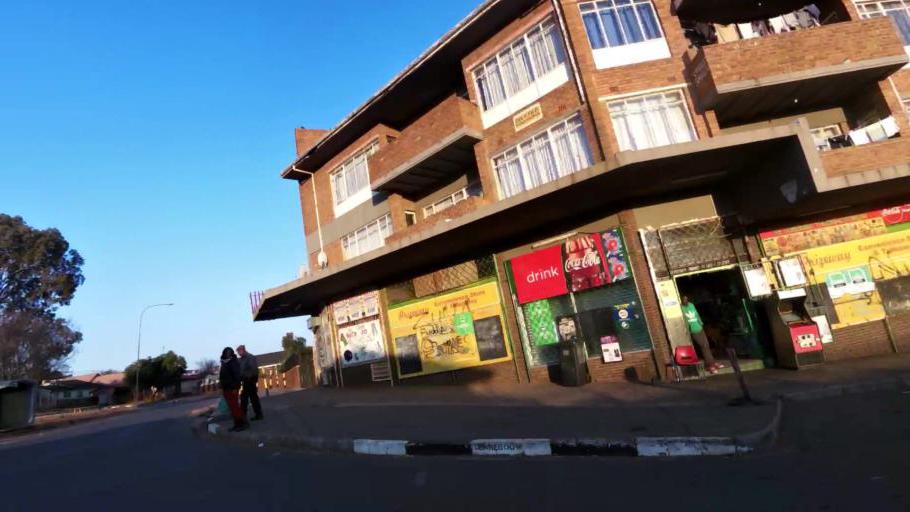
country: ZA
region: Gauteng
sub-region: City of Johannesburg Metropolitan Municipality
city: Roodepoort
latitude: -26.1843
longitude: 27.9505
